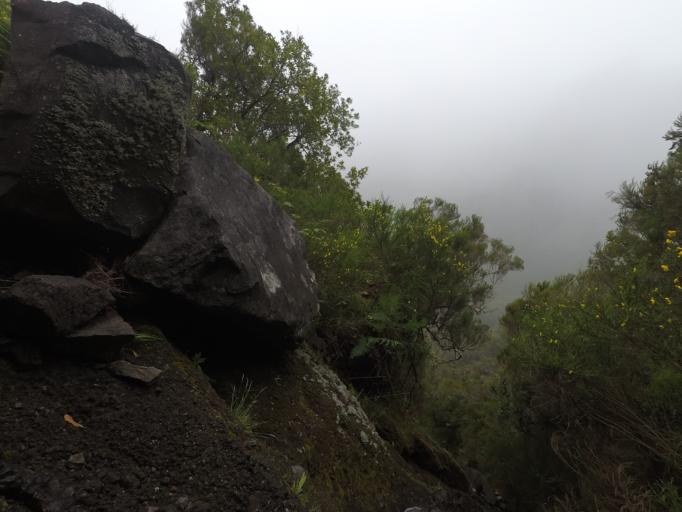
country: PT
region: Madeira
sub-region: Sao Vicente
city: Sao Vicente
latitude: 32.7676
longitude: -17.0567
